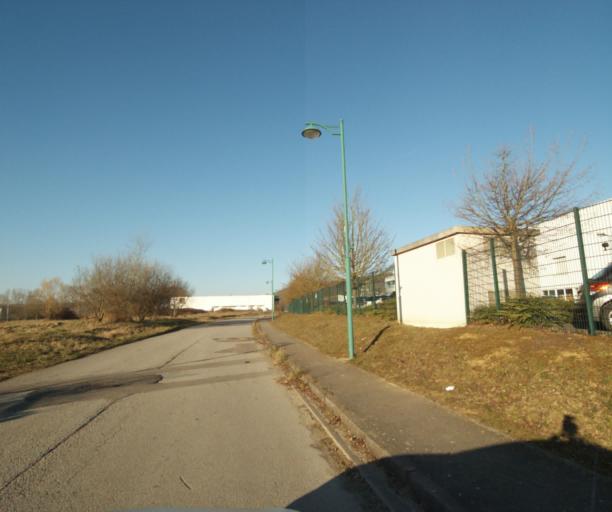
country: FR
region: Lorraine
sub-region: Departement de Meurthe-et-Moselle
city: Malzeville
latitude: 48.7172
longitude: 6.1760
